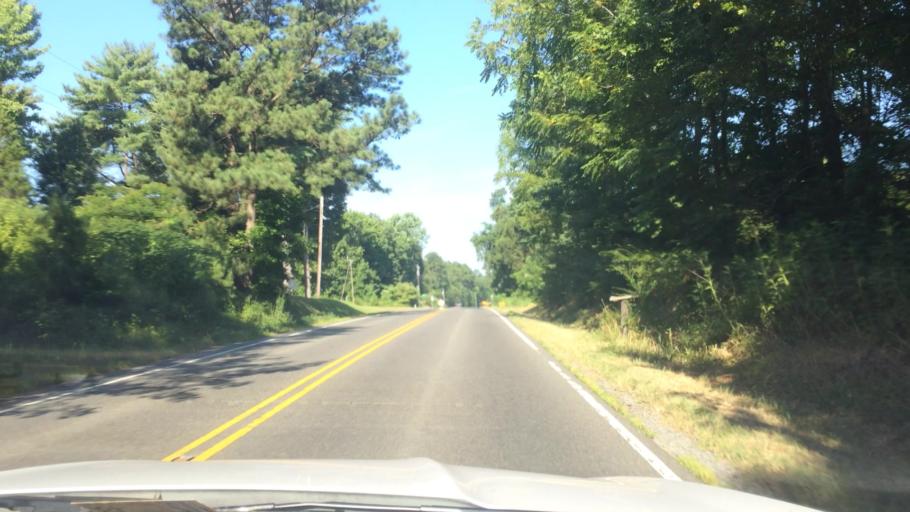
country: US
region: Virginia
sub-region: Lancaster County
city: Lancaster
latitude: 37.7690
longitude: -76.4976
